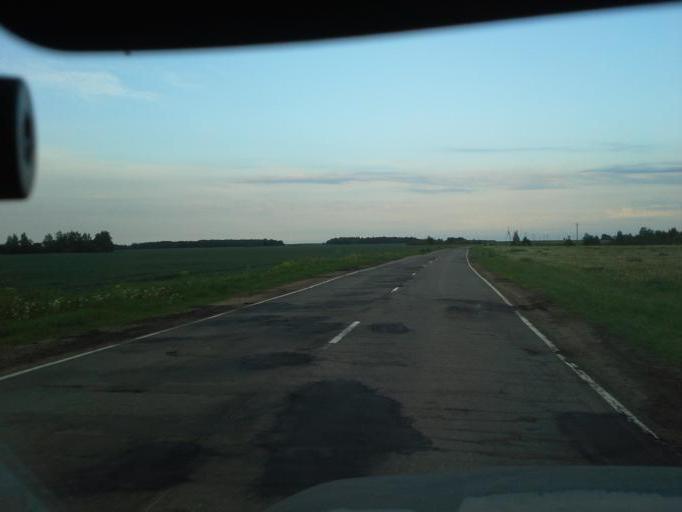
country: RU
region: Ivanovo
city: Gavrilov Posad
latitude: 56.5472
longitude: 40.1876
